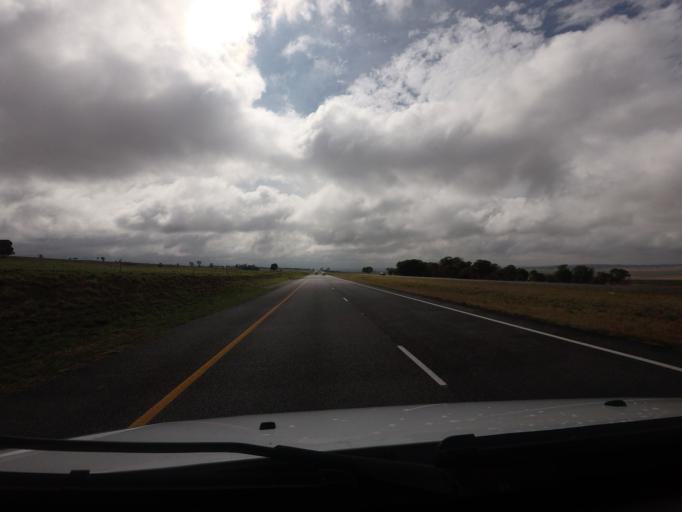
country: ZA
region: Gauteng
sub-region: City of Tshwane Metropolitan Municipality
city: Bronkhorstspruit
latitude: -25.7993
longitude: 28.6352
